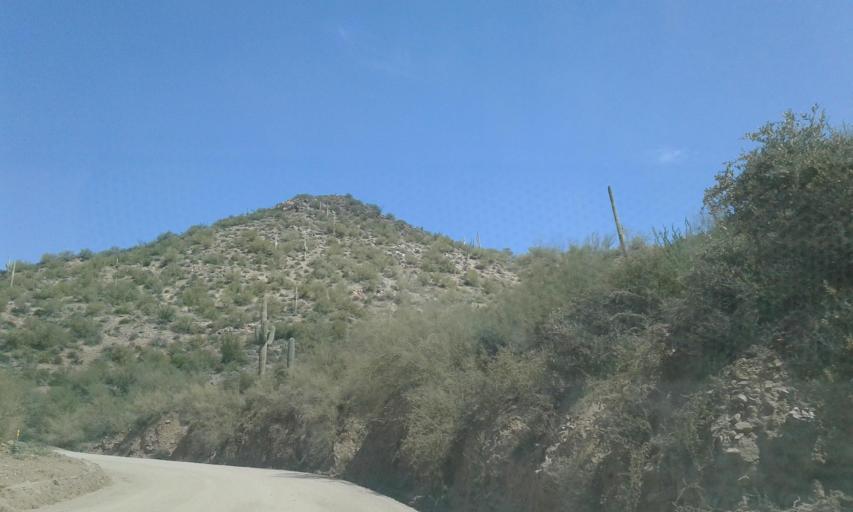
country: US
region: Arizona
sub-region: Gila County
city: Tonto Basin
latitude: 33.6362
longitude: -111.1973
